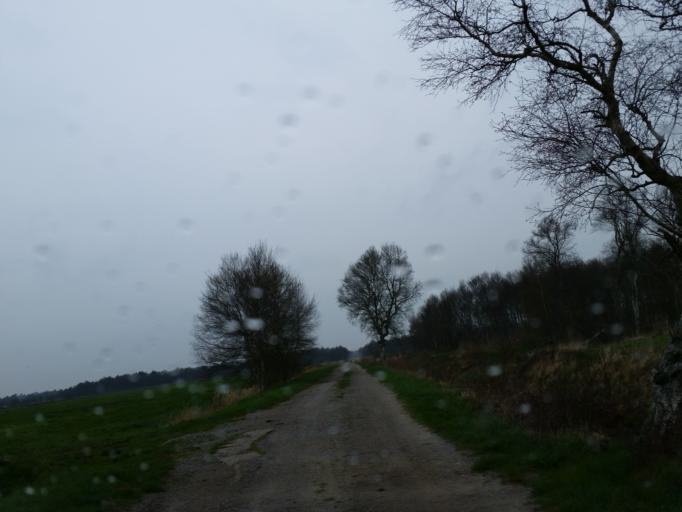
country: DE
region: Lower Saxony
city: Armstorf
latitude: 53.5938
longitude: 9.0058
